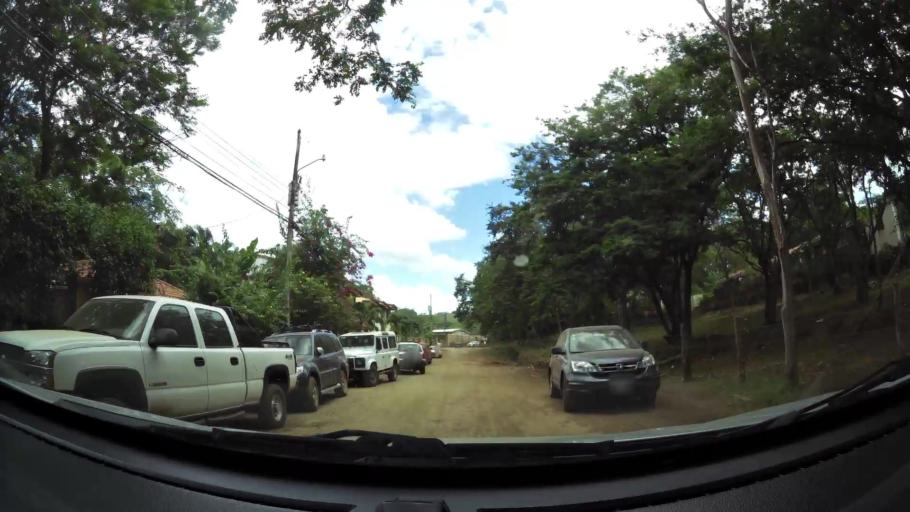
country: CR
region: Guanacaste
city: Santa Cruz
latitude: 10.2949
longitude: -85.8407
